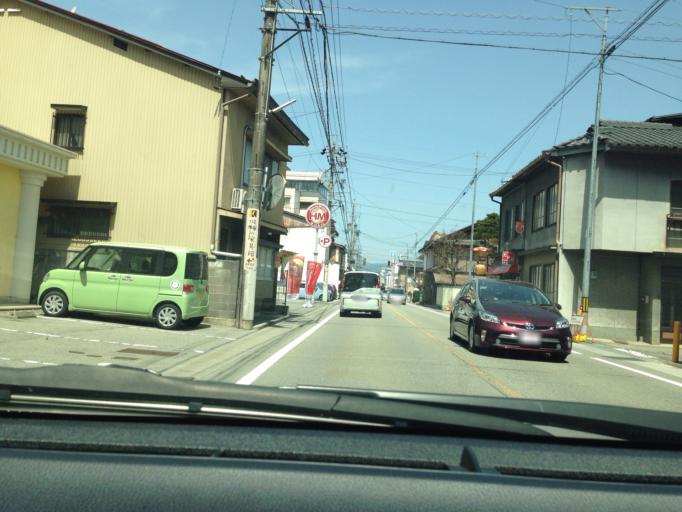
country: JP
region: Gifu
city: Takayama
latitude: 36.1352
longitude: 137.2554
